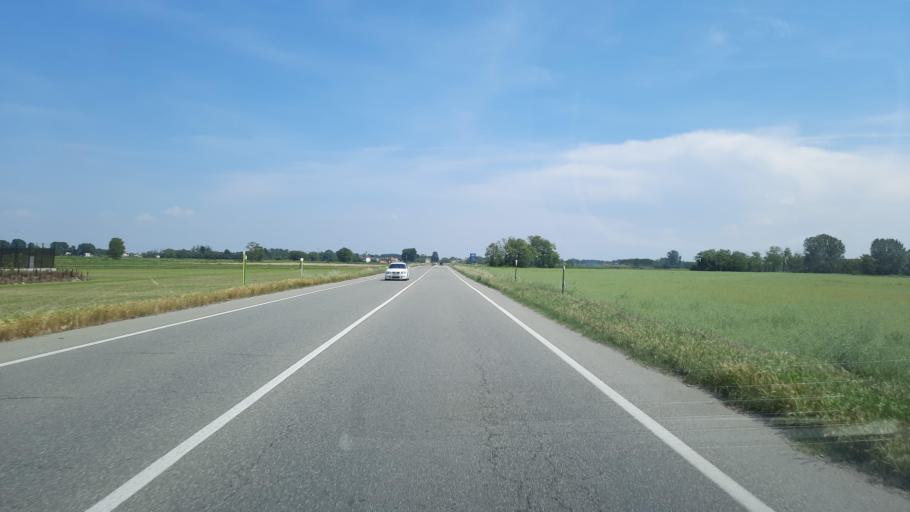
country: IT
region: Lombardy
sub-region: Provincia di Pavia
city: Mortara
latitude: 45.2438
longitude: 8.7727
